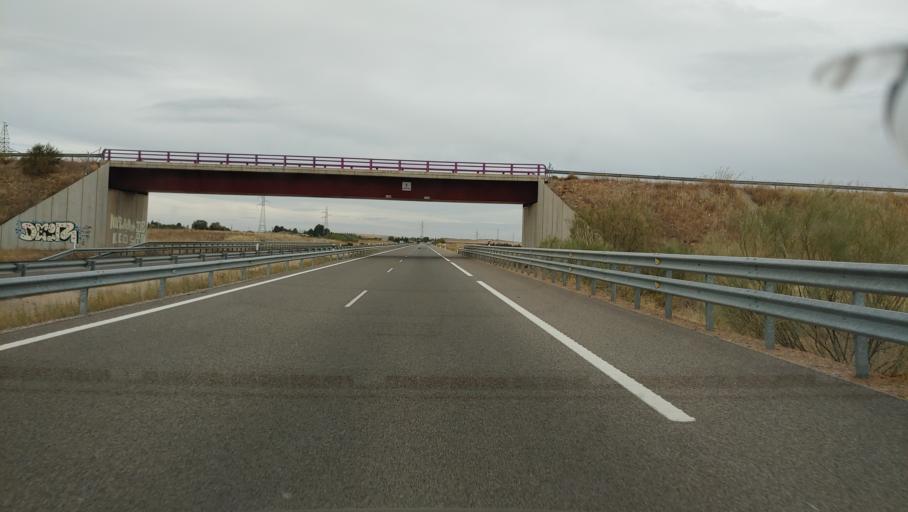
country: ES
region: Castille-La Mancha
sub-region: Provincia de Ciudad Real
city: Miguelturra
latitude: 38.9494
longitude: -3.9050
